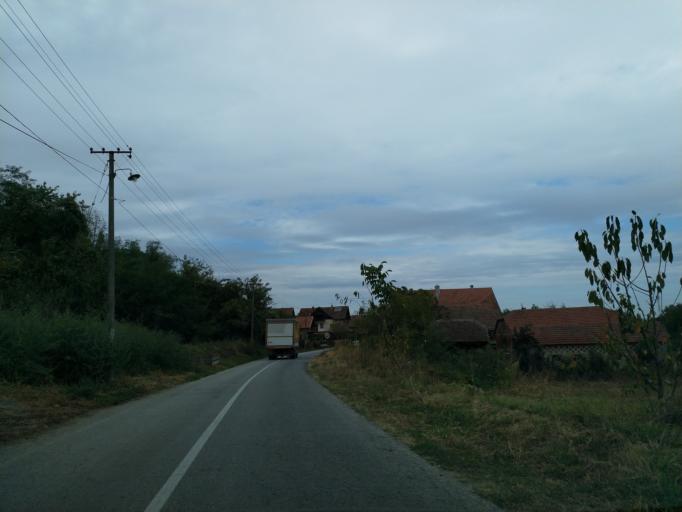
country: RS
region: Central Serbia
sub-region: Pomoravski Okrug
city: Cuprija
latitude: 43.8610
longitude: 21.3237
